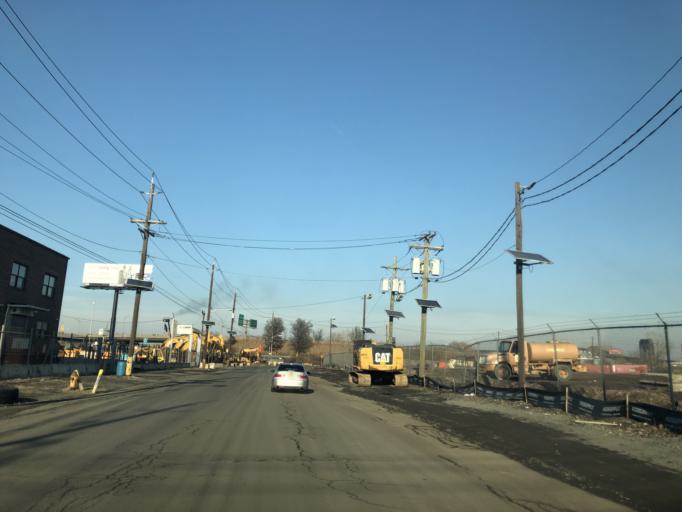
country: US
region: New Jersey
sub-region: Hudson County
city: Harrison
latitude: 40.7263
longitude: -74.1287
